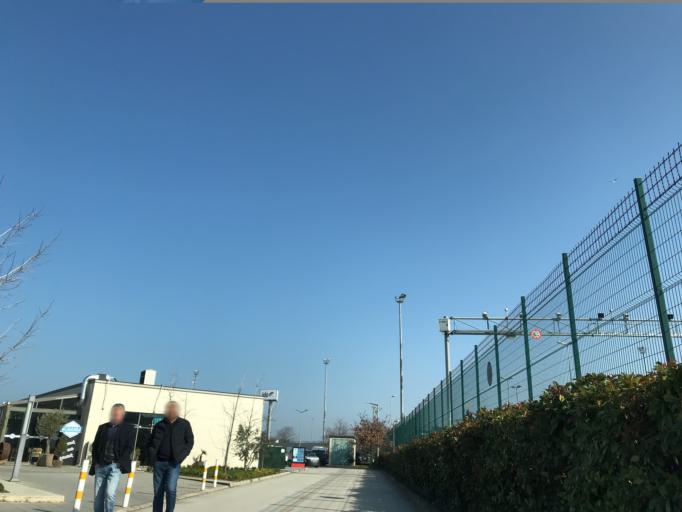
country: TR
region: Yalova
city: Yalova
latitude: 40.6599
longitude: 29.2768
